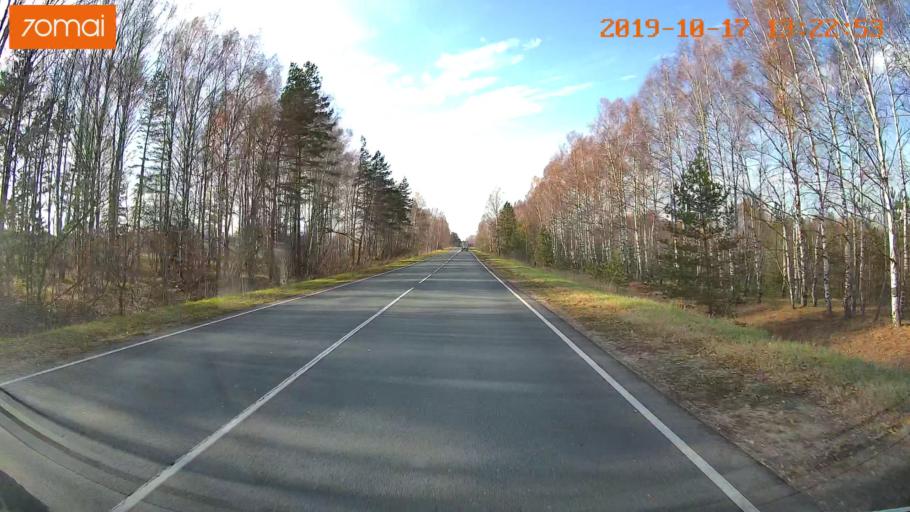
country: RU
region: Rjazan
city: Gus'-Zheleznyy
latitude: 55.0873
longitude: 40.9917
